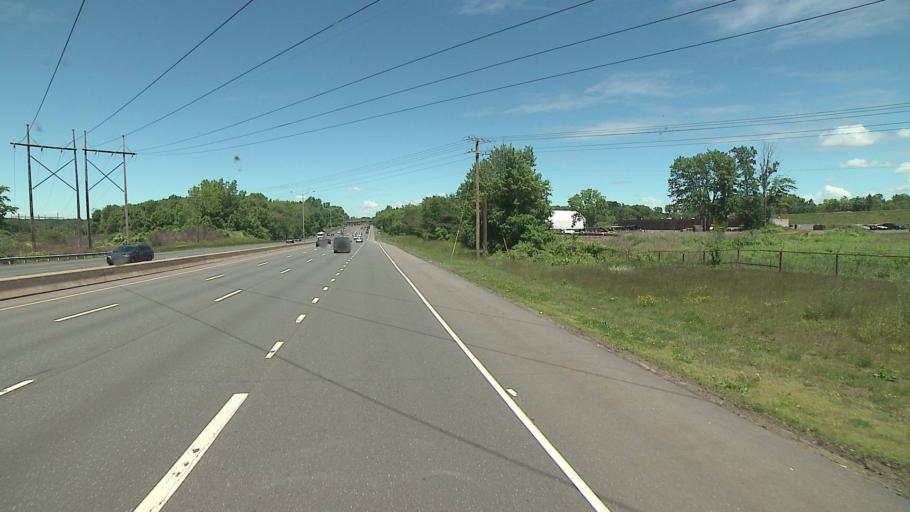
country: US
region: Connecticut
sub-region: Hartford County
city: Windsor Locks
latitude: 41.9324
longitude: -72.6081
